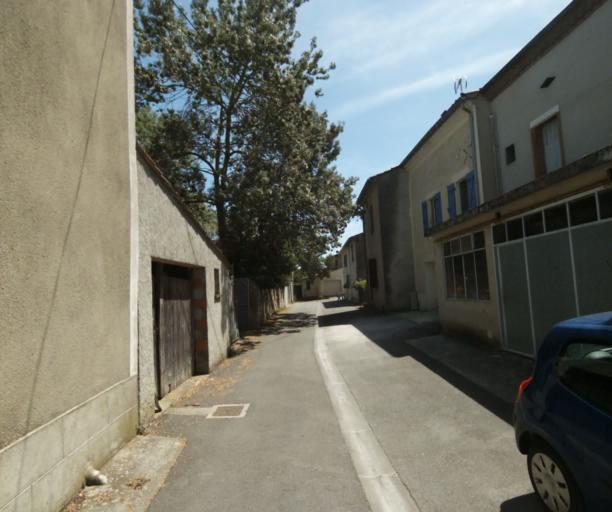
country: FR
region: Midi-Pyrenees
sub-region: Departement de la Haute-Garonne
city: Revel
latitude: 43.4907
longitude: 2.0213
